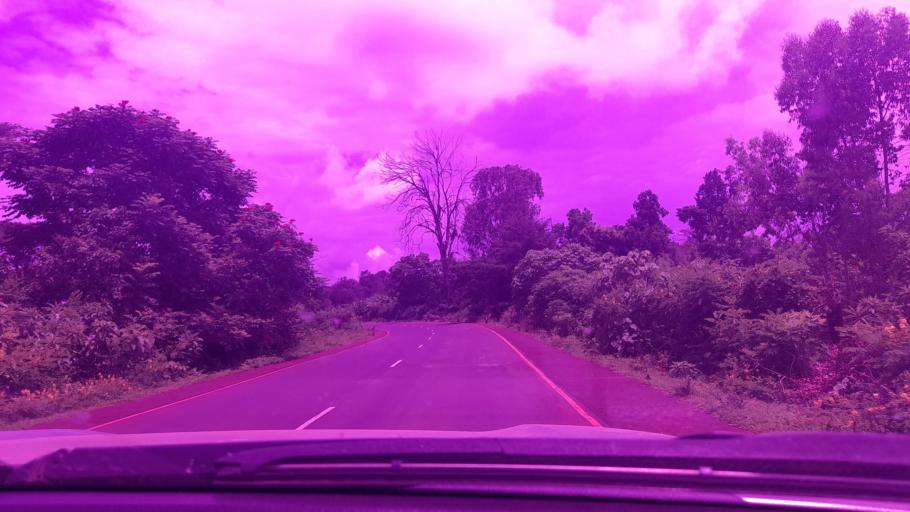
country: ET
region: Oromiya
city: Metu
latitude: 8.3385
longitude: 35.7220
